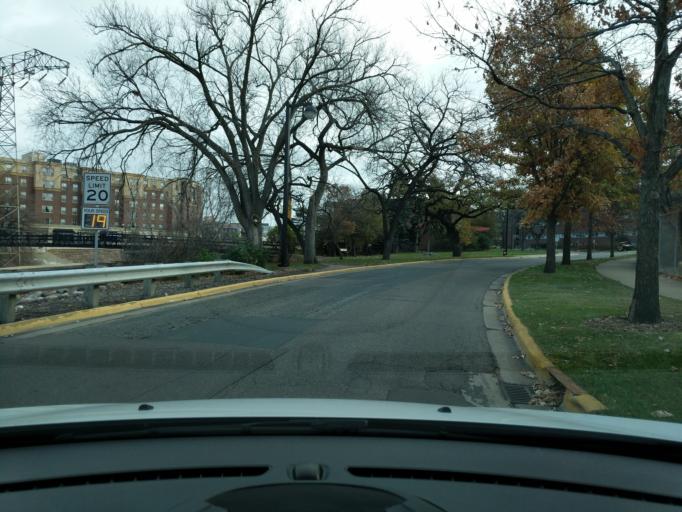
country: US
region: Minnesota
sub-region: Hennepin County
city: Minneapolis
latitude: 44.9793
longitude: -93.2390
